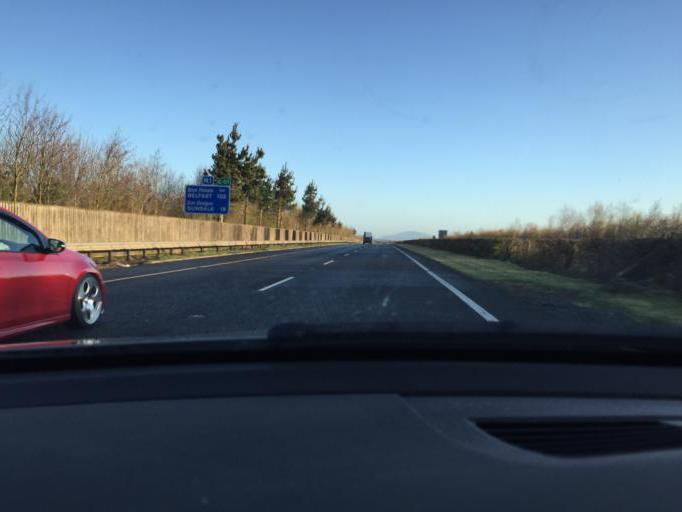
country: IE
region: Leinster
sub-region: Lu
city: Dunleer
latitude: 53.8675
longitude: -6.4288
